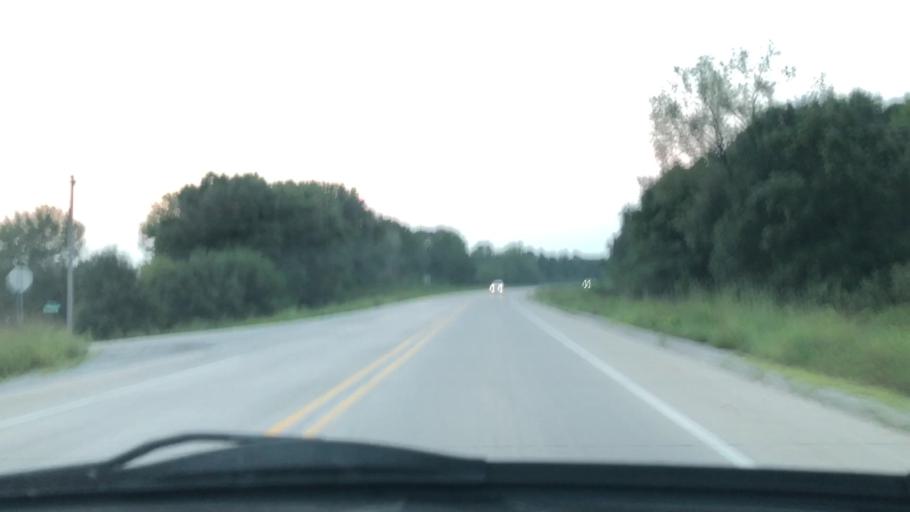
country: US
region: Iowa
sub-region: Johnson County
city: North Liberty
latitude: 41.8142
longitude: -91.6659
